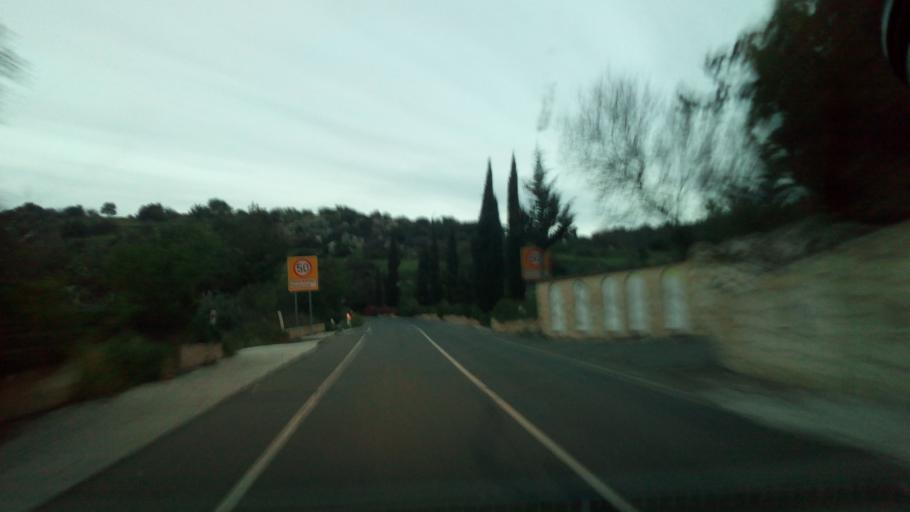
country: CY
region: Pafos
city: Polis
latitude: 34.9859
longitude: 32.4885
